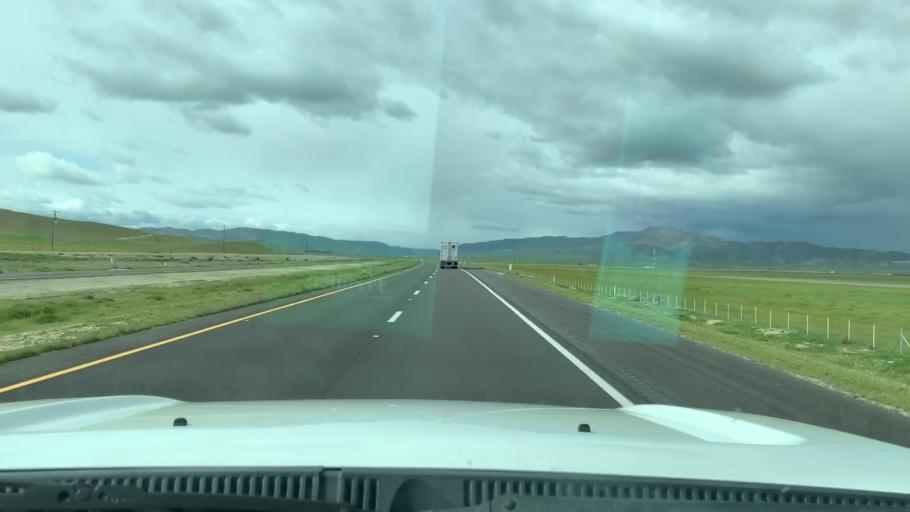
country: US
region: California
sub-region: Kern County
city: Lost Hills
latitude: 35.6445
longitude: -120.0260
